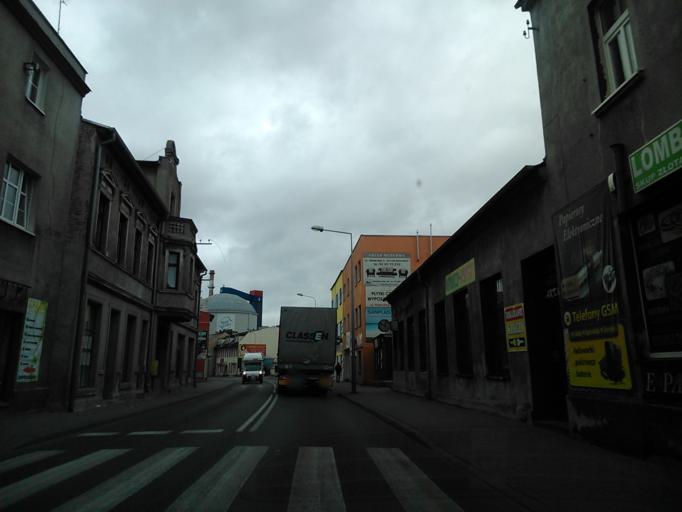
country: PL
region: Kujawsko-Pomorskie
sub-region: Powiat inowroclawski
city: Kruszwica
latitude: 52.6745
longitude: 18.3214
